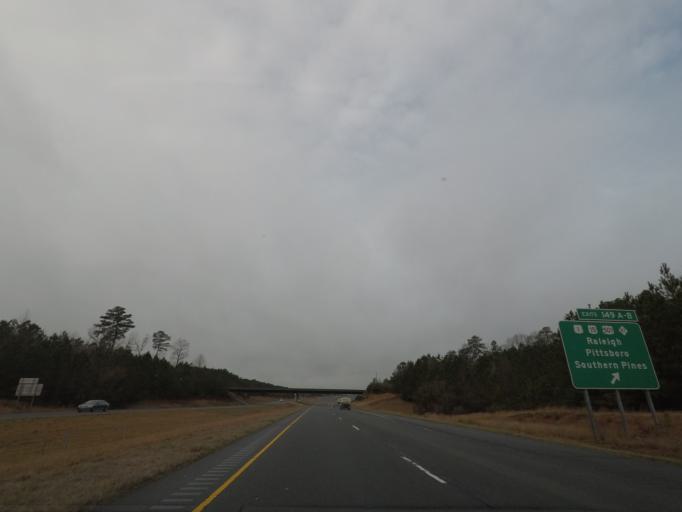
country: US
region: North Carolina
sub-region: Lee County
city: Sanford
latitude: 35.5086
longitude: -79.1764
